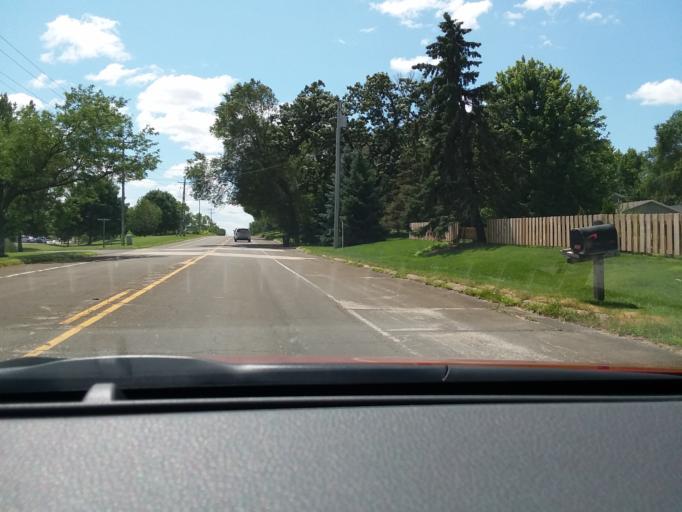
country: US
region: Wisconsin
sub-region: Dane County
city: Windsor
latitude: 43.2119
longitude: -89.3432
